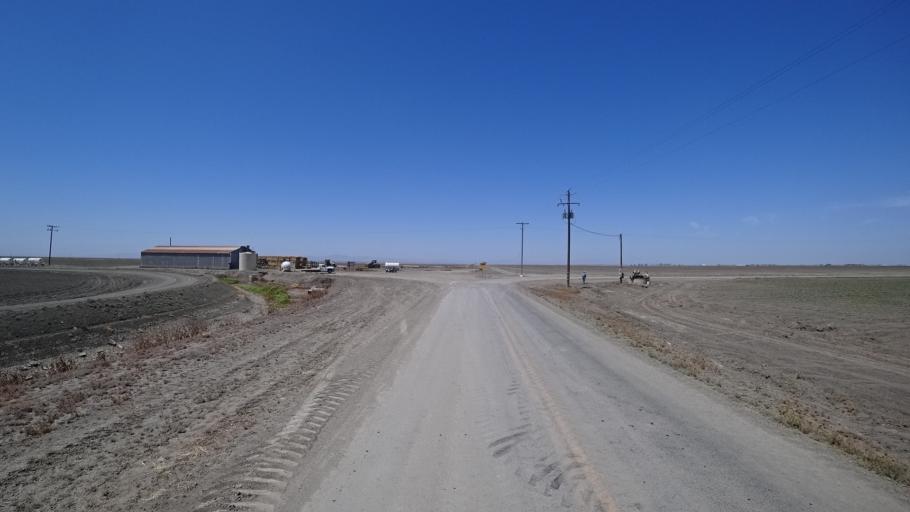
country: US
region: California
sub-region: Kings County
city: Stratford
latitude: 36.1232
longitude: -119.7334
